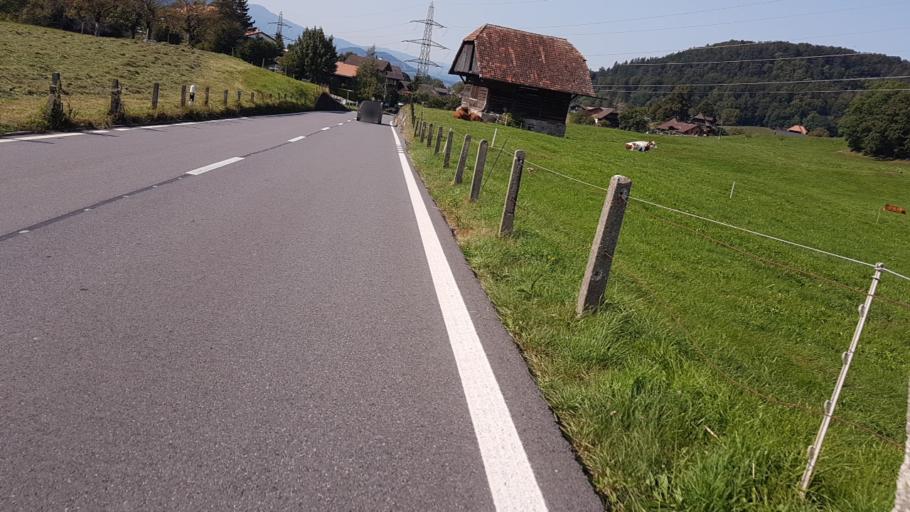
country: CH
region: Bern
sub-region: Frutigen-Niedersimmental District
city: Aeschi
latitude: 46.6669
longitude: 7.6831
